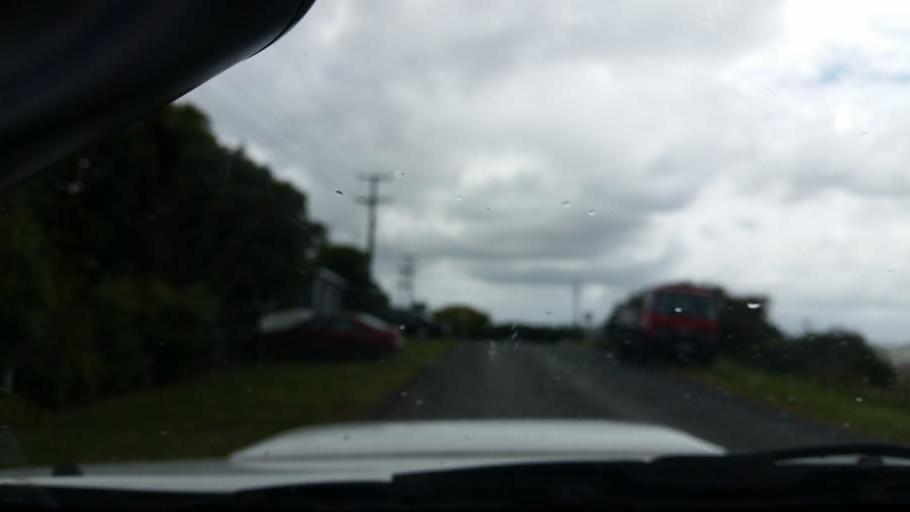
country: NZ
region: Northland
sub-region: Whangarei
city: Ruakaka
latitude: -36.1065
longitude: 174.3479
